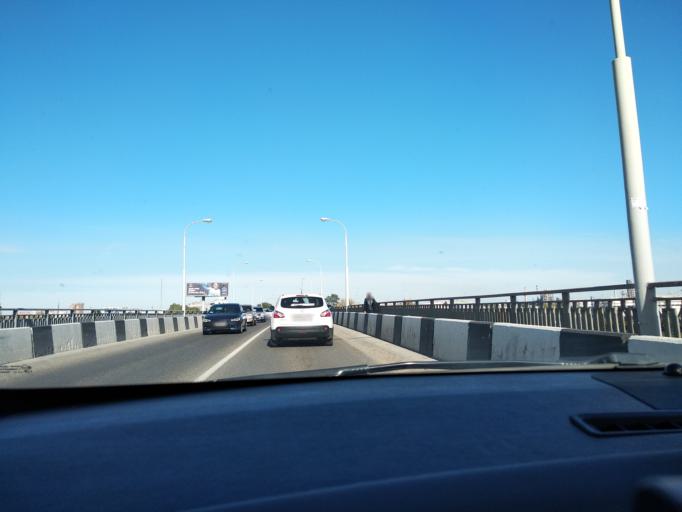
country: RU
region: Adygeya
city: Yablonovskiy
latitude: 44.9953
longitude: 38.9571
